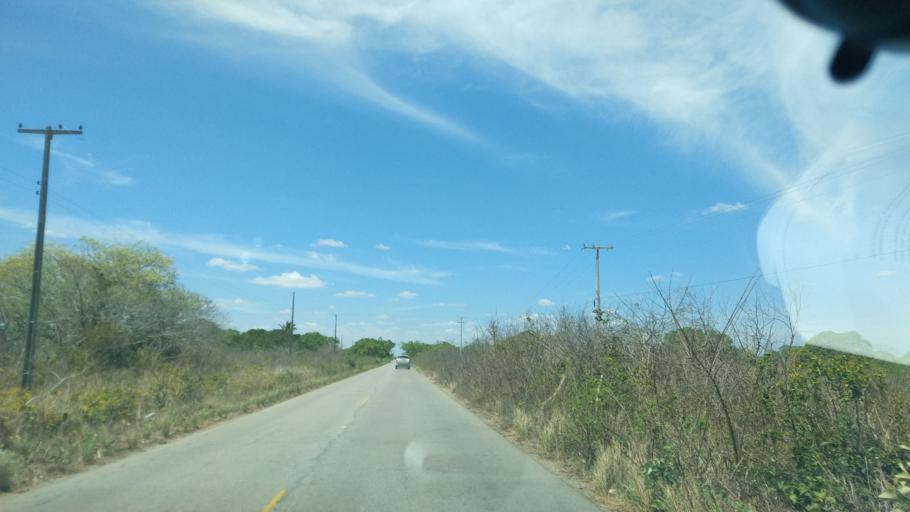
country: BR
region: Rio Grande do Norte
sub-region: Sao Paulo Do Potengi
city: Sao Paulo do Potengi
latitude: -5.9301
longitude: -35.5686
